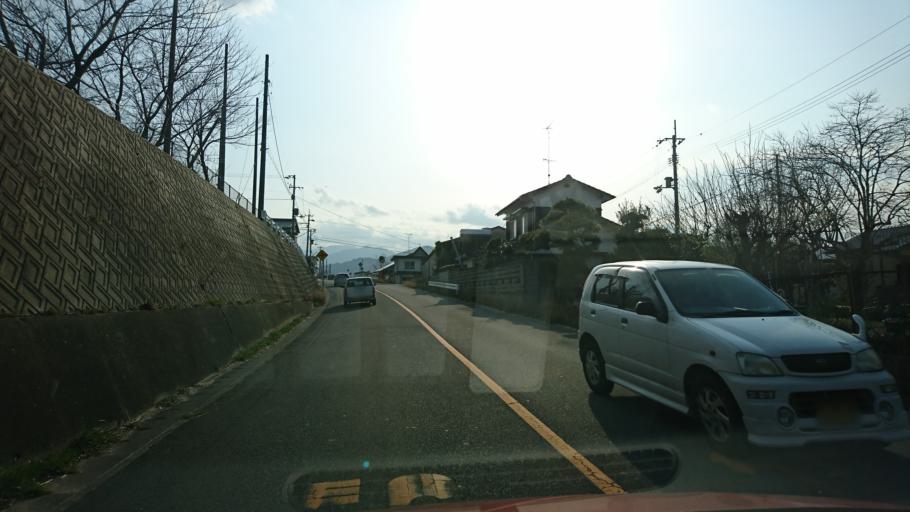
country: JP
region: Ehime
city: Saijo
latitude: 34.0291
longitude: 133.0148
